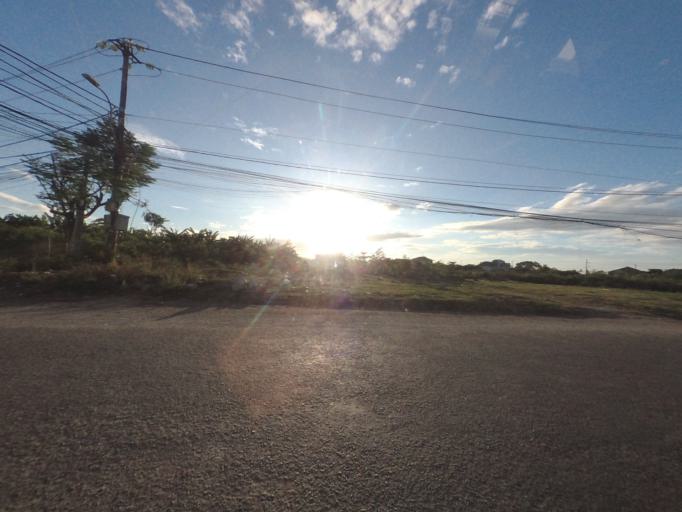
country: VN
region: Thua Thien-Hue
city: Hue
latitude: 16.4910
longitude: 107.5834
